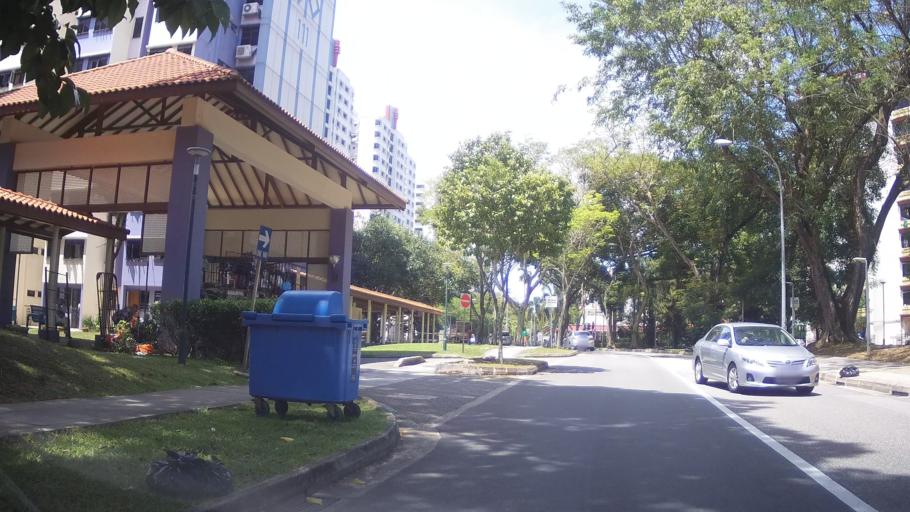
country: SG
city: Singapore
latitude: 1.3344
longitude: 103.7239
